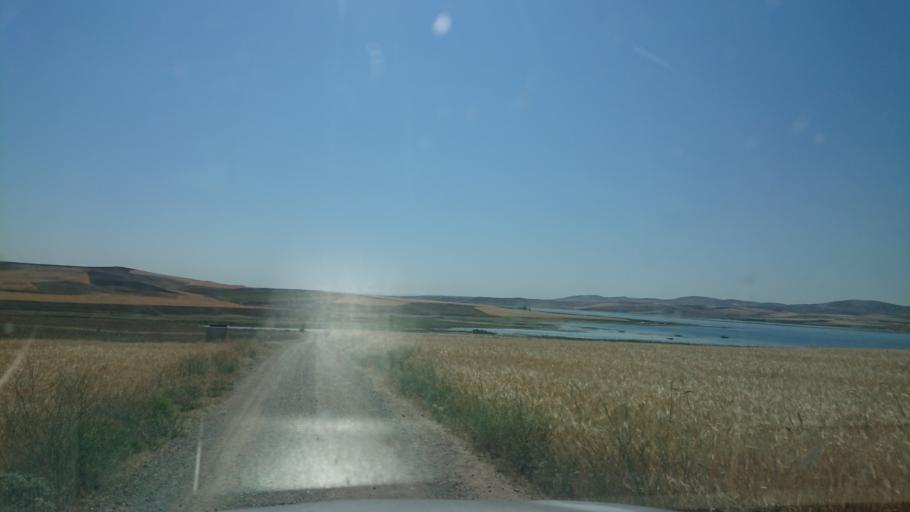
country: TR
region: Aksaray
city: Sariyahsi
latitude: 39.0554
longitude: 33.8954
